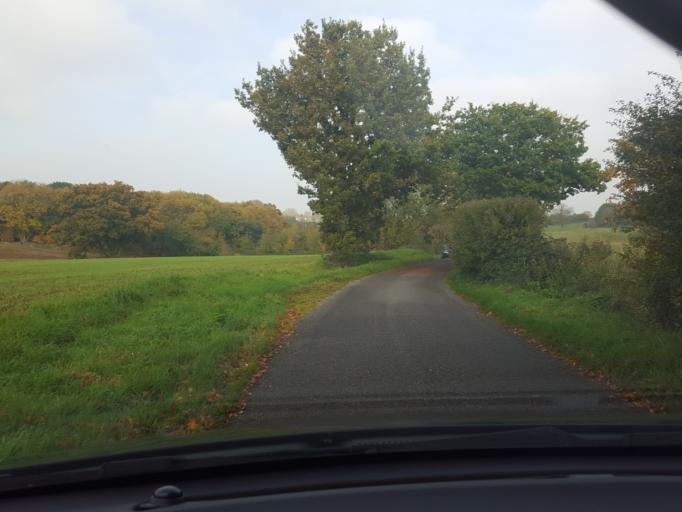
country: GB
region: England
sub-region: Essex
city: Mistley
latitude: 51.9350
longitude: 1.1613
